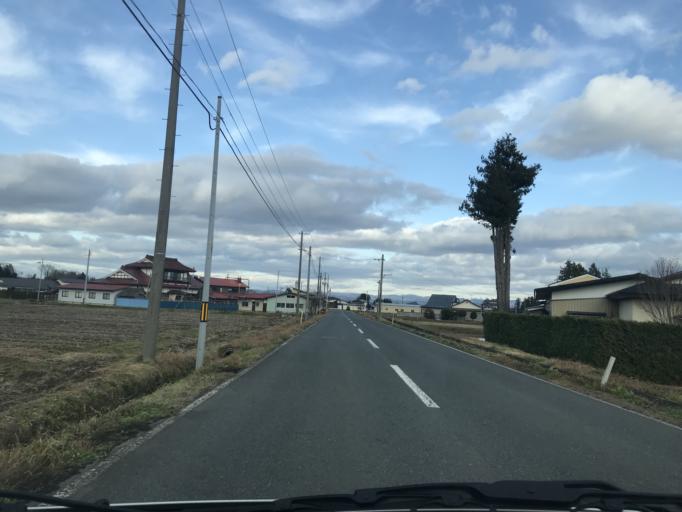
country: JP
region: Iwate
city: Mizusawa
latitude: 39.1714
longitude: 141.0901
